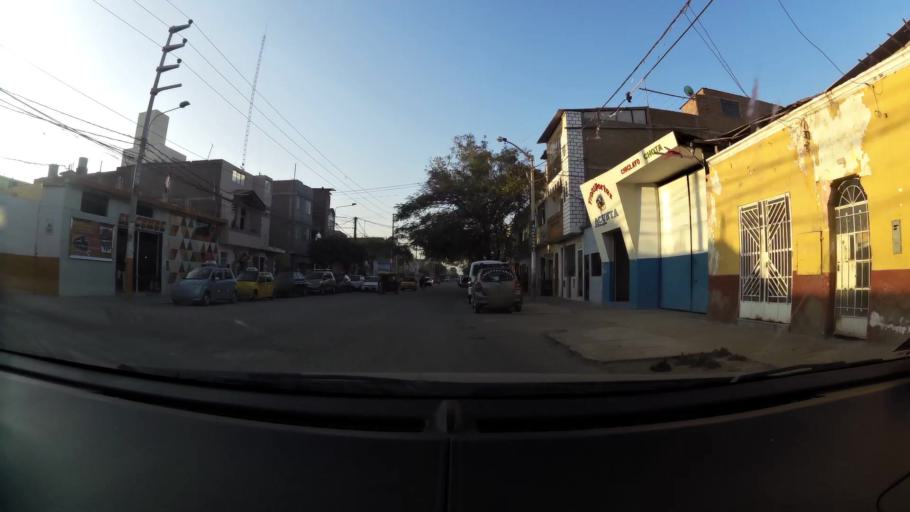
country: PE
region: Lambayeque
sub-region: Provincia de Chiclayo
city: Santa Rosa
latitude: -6.7706
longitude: -79.8330
